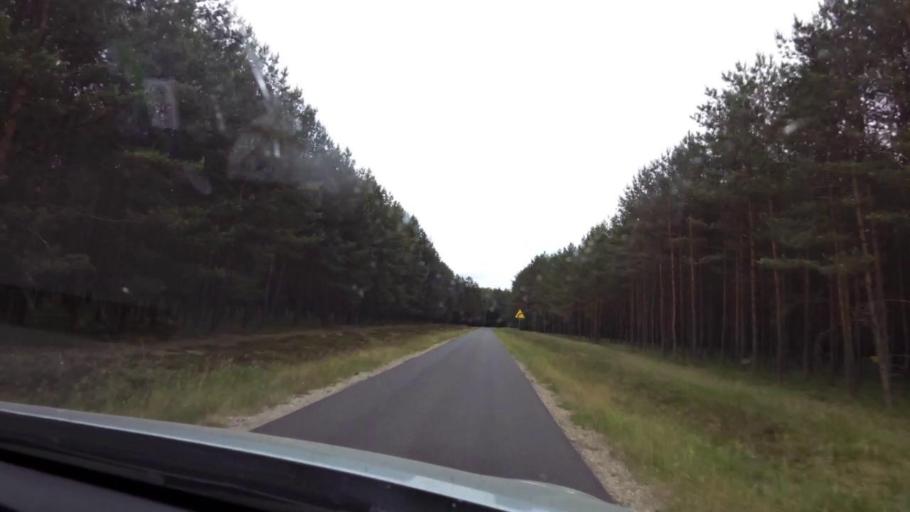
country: PL
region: Pomeranian Voivodeship
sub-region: Powiat bytowski
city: Trzebielino
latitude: 54.1971
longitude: 17.0404
